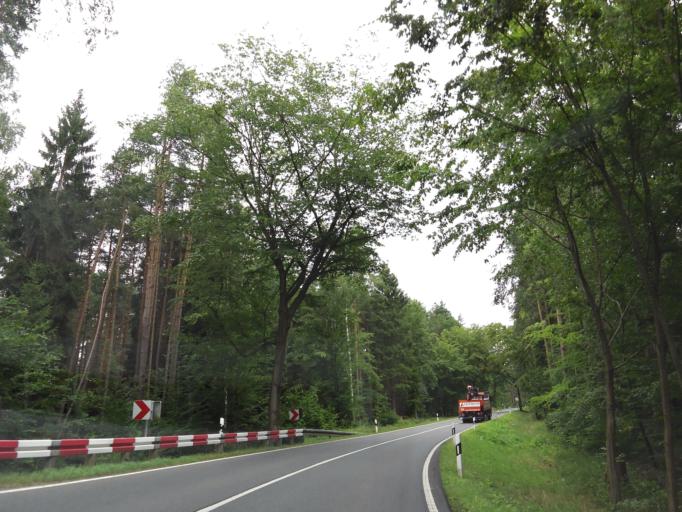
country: DE
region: Thuringia
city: Hainspitz
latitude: 50.9393
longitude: 11.8509
